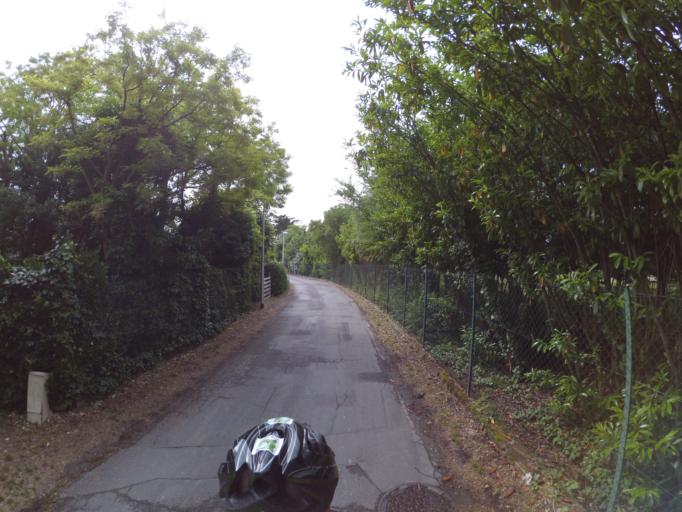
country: FR
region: Poitou-Charentes
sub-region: Departement de la Charente-Maritime
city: Angoulins
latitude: 46.0961
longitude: -1.1029
